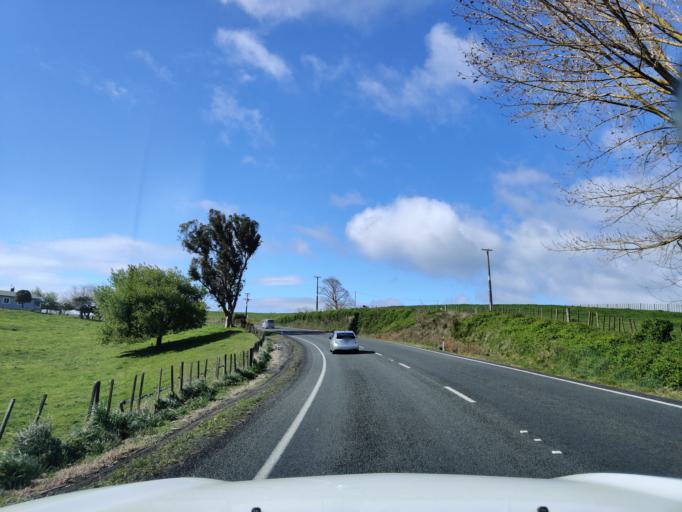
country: NZ
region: Waikato
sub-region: Otorohanga District
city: Otorohanga
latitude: -38.0939
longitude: 175.1828
